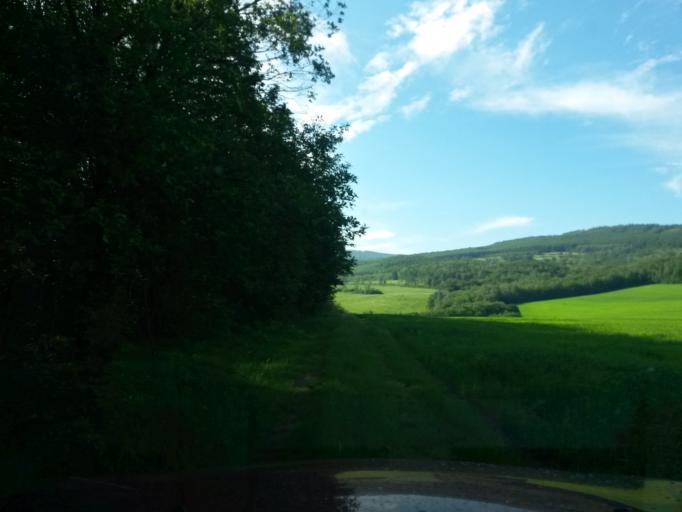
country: SK
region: Kosicky
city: Moldava nad Bodvou
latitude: 48.7281
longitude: 21.0827
